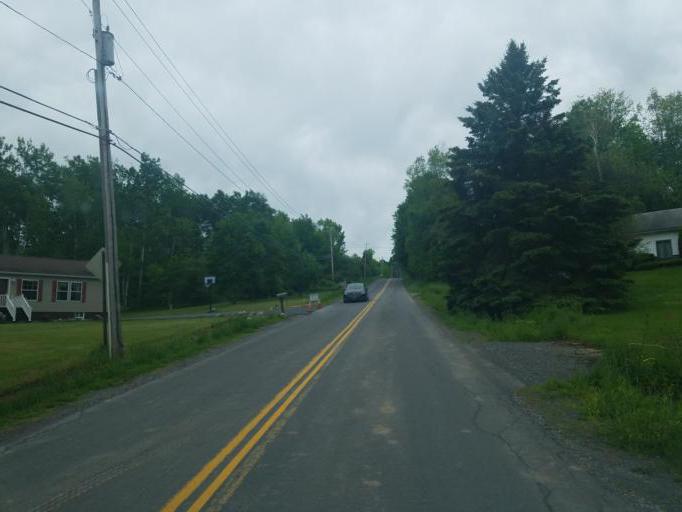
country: US
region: New York
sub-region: Herkimer County
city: Ilion
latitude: 42.9801
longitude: -75.0238
